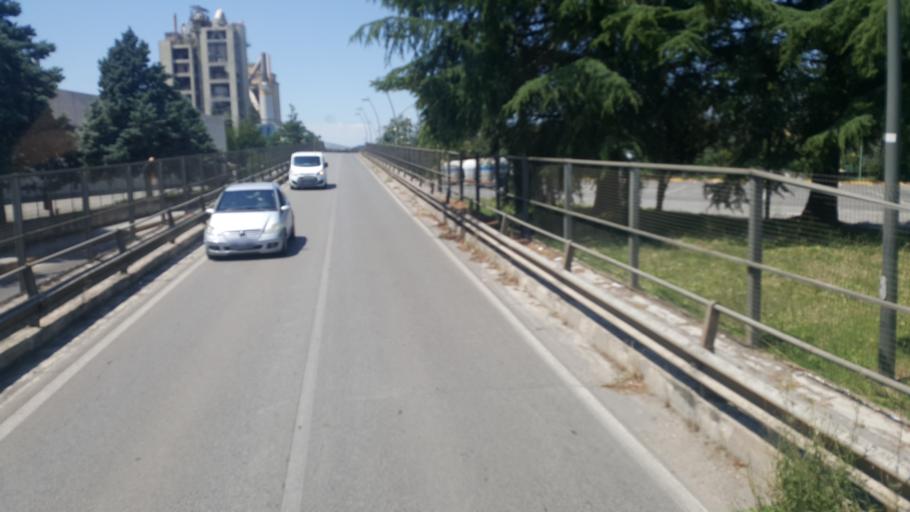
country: IT
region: Latium
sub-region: Citta metropolitana di Roma Capitale
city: Colleferro
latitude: 41.7350
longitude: 13.0084
